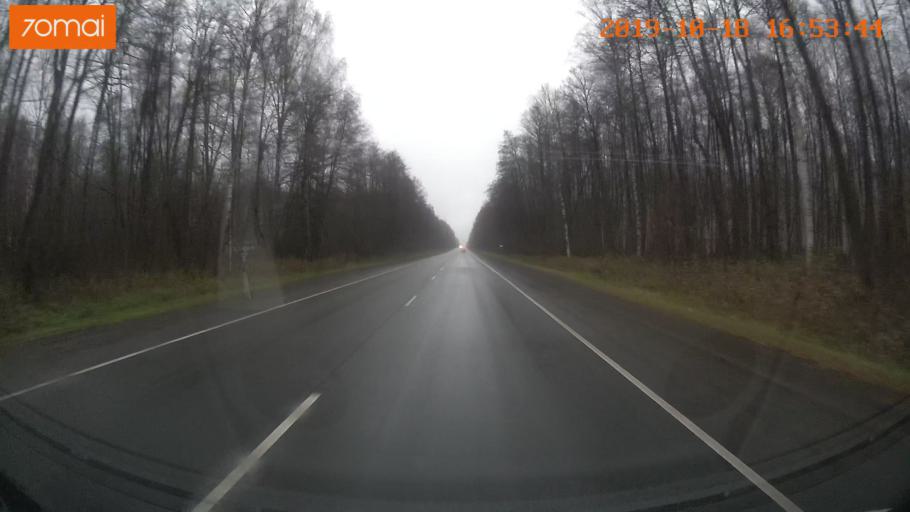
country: RU
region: Ivanovo
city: Nerl'
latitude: 56.6191
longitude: 40.5630
